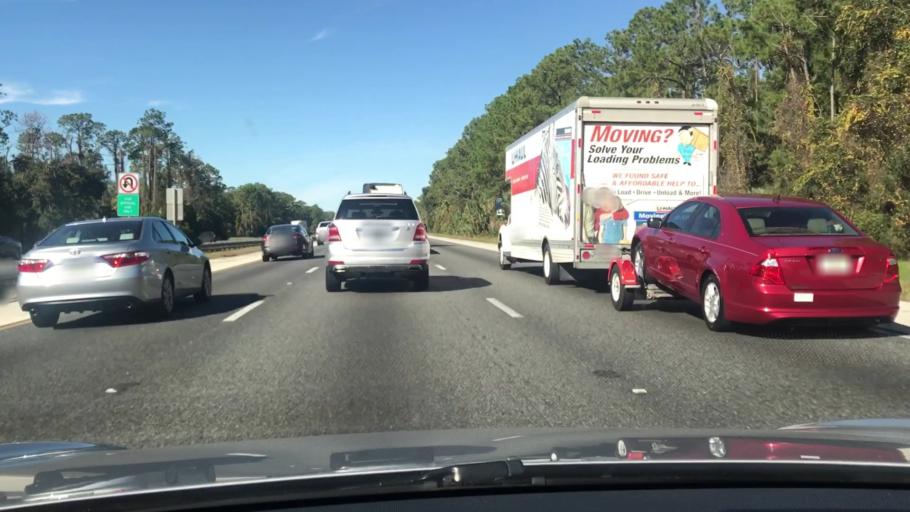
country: US
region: Florida
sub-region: Volusia County
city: Ormond-by-the-Sea
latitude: 29.3770
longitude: -81.1434
